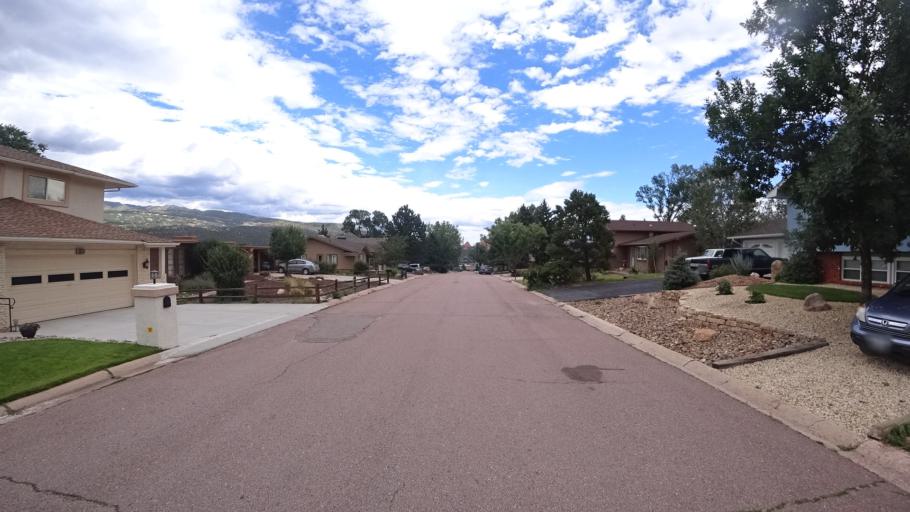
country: US
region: Colorado
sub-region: El Paso County
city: Manitou Springs
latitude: 38.8538
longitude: -104.8902
